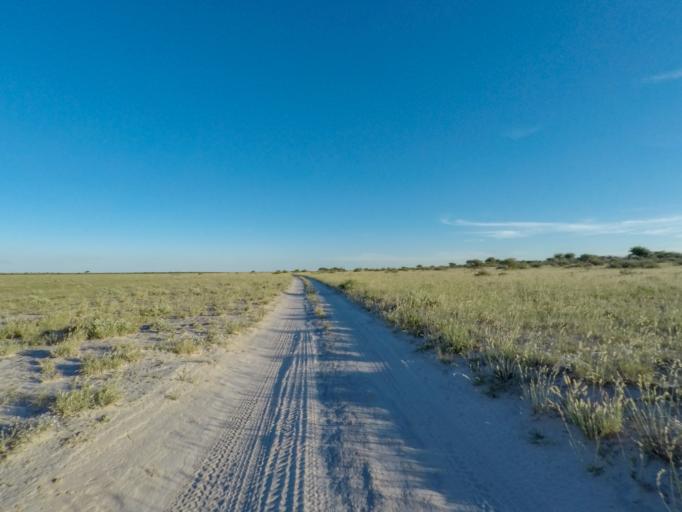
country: BW
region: Central
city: Rakops
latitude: -21.4020
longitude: 23.7954
